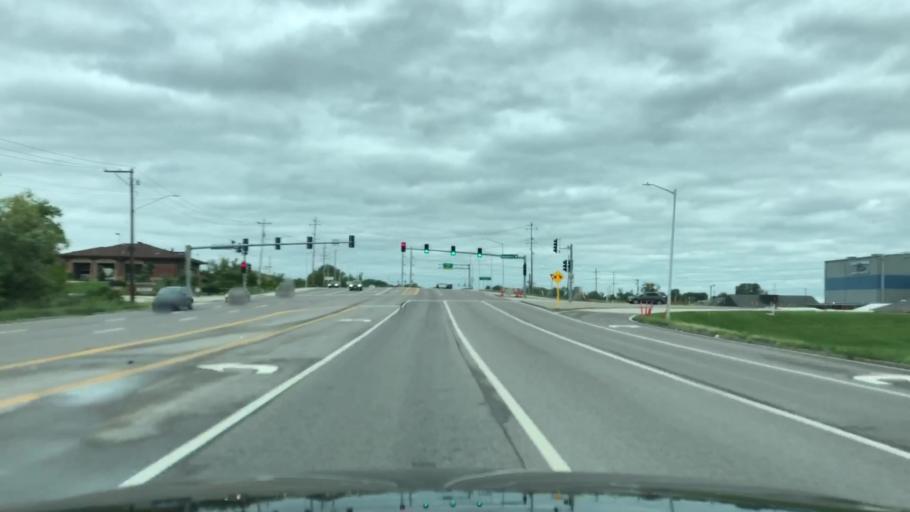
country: US
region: Missouri
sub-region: Saint Charles County
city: Saint Charles
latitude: 38.7448
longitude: -90.4663
